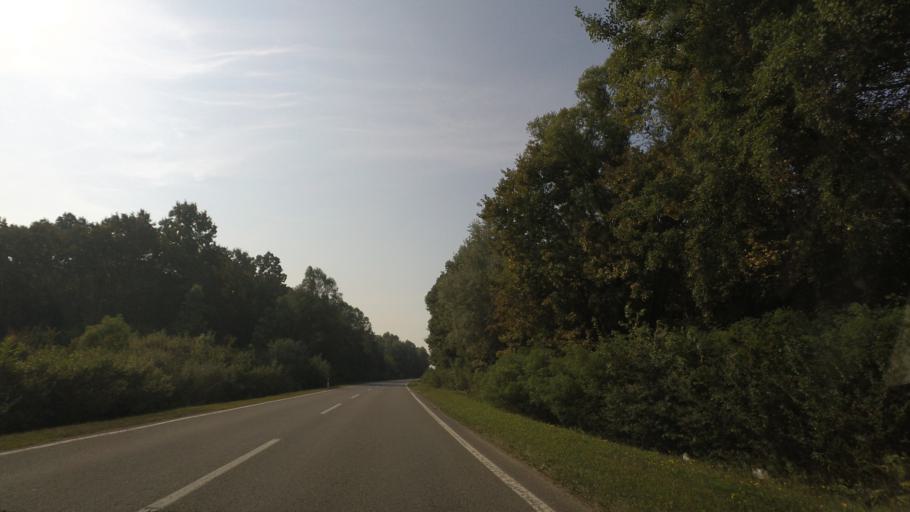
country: HR
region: Sisacko-Moslavacka
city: Novska
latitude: 45.3222
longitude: 16.9489
